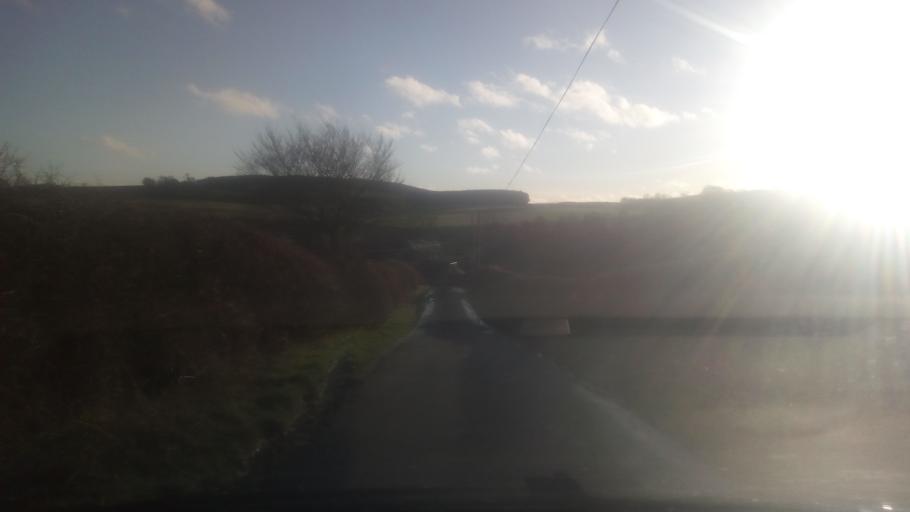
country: GB
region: Scotland
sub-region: The Scottish Borders
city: Jedburgh
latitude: 55.4694
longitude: -2.4799
